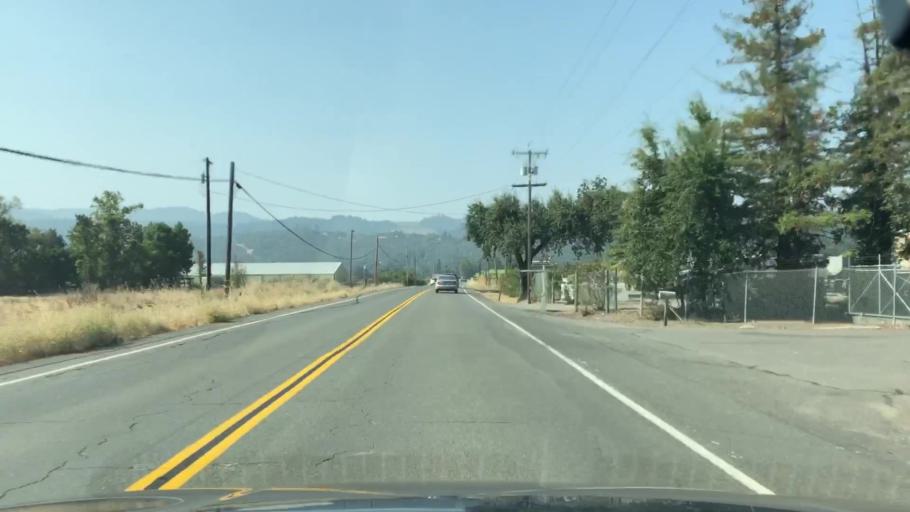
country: US
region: California
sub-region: Napa County
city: Calistoga
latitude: 38.5994
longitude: -122.5994
